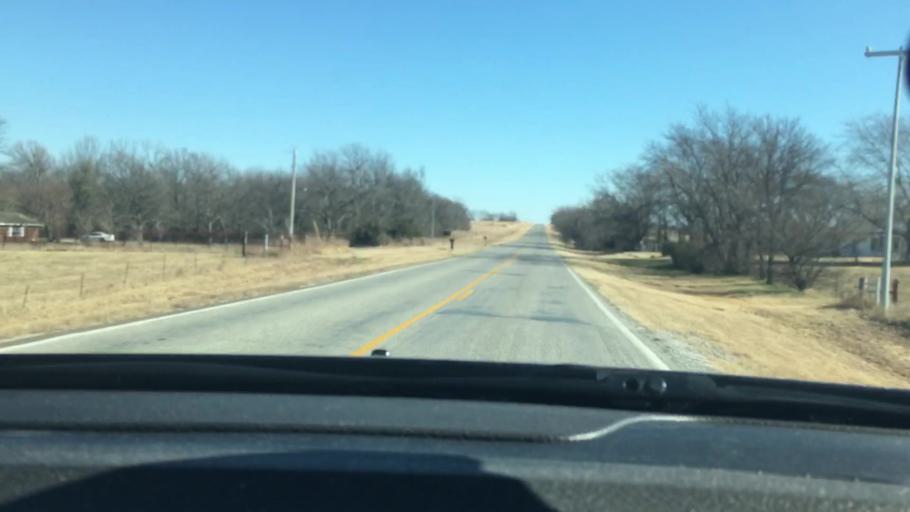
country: US
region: Oklahoma
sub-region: Garvin County
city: Wynnewood
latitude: 34.6515
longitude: -97.1038
